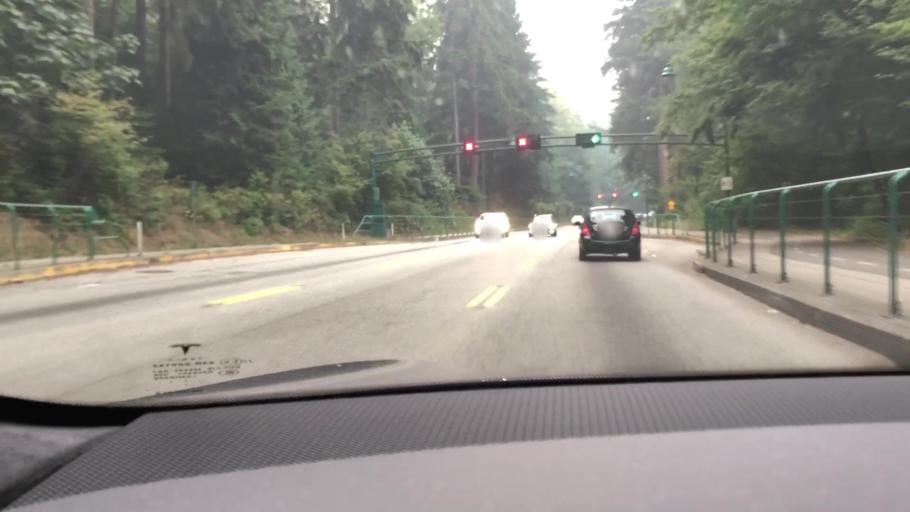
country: CA
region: British Columbia
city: West End
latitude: 49.3048
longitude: -123.1453
